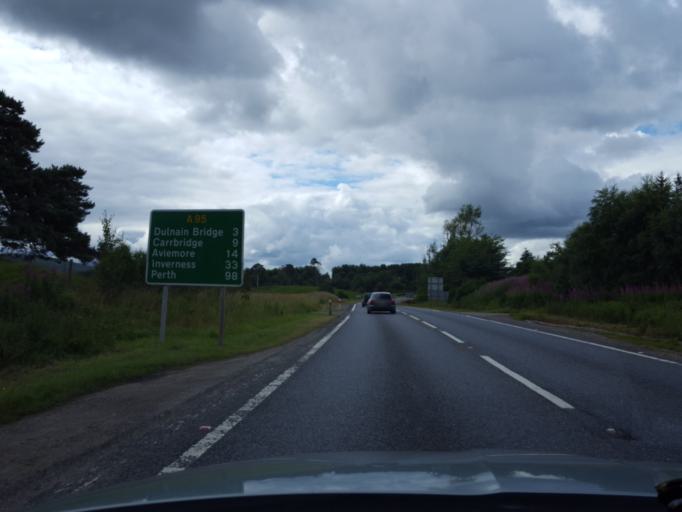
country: GB
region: Scotland
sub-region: Highland
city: Grantown on Spey
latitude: 57.3191
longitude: -3.6201
